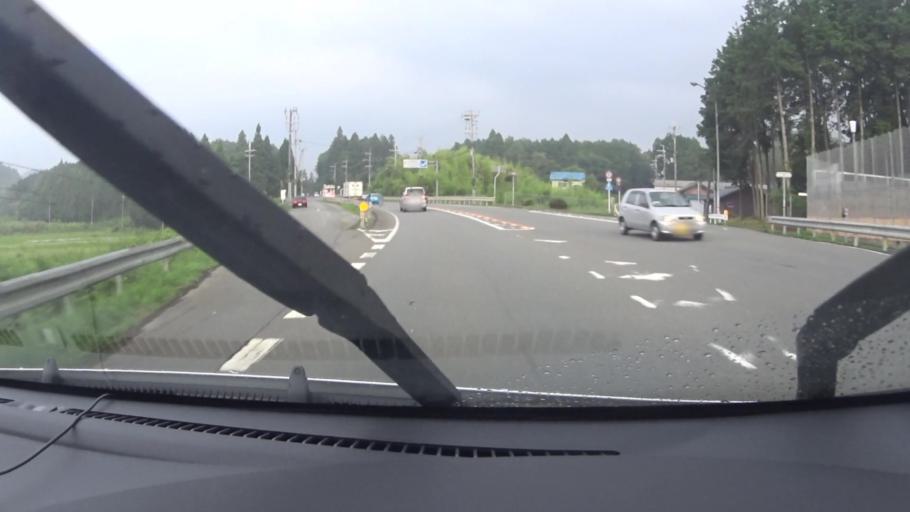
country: JP
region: Kyoto
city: Ayabe
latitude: 35.1955
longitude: 135.4182
